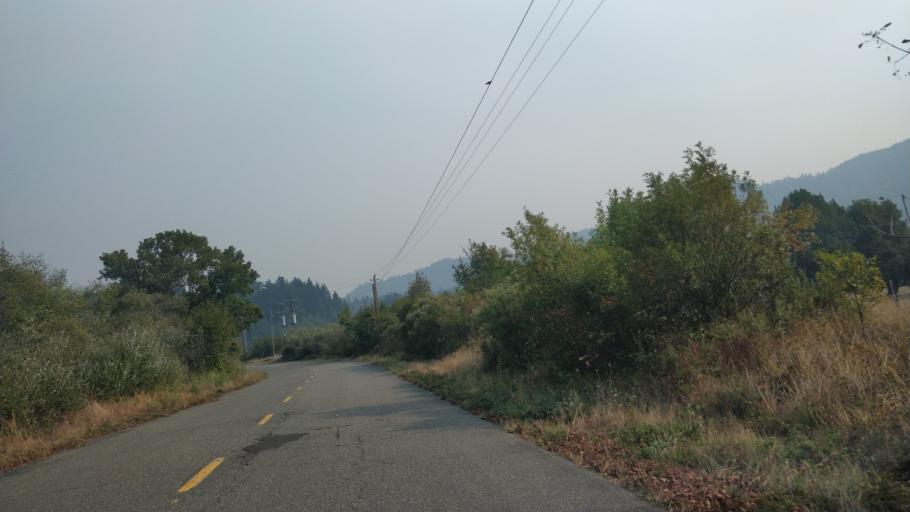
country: US
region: California
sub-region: Humboldt County
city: Rio Dell
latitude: 40.2797
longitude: -124.2472
